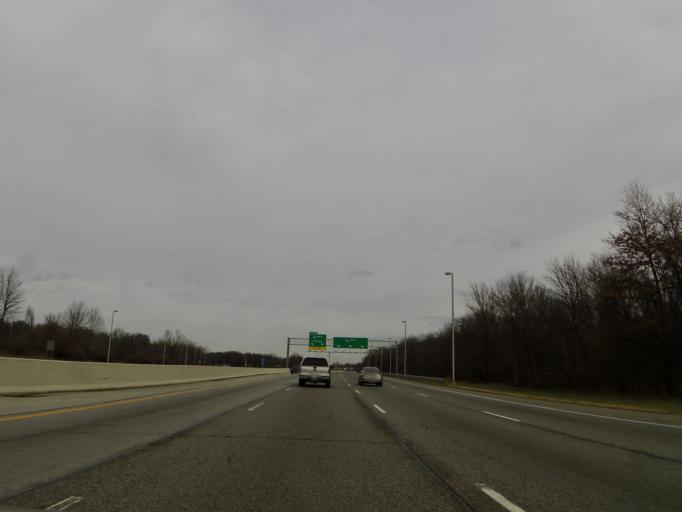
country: US
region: Indiana
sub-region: Marion County
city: Speedway
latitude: 39.8553
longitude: -86.2762
